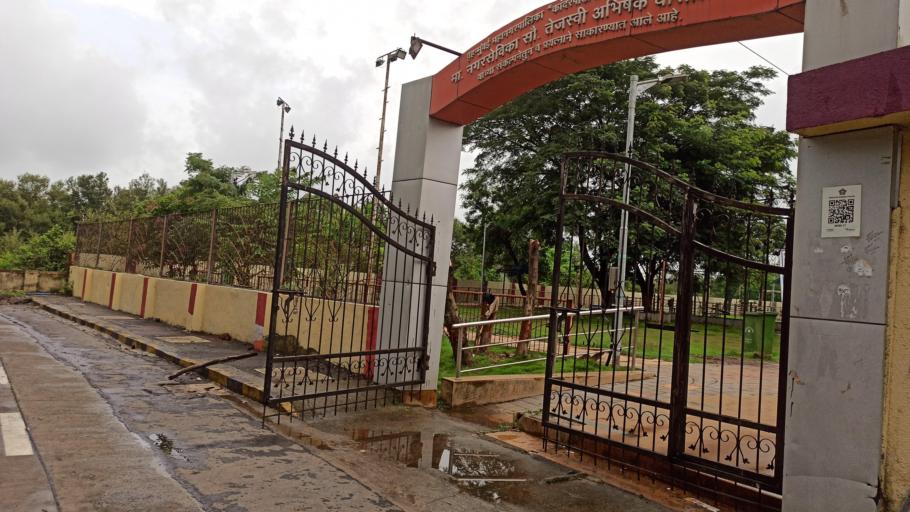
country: IN
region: Maharashtra
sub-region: Mumbai Suburban
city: Borivli
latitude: 19.2612
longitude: 72.8503
